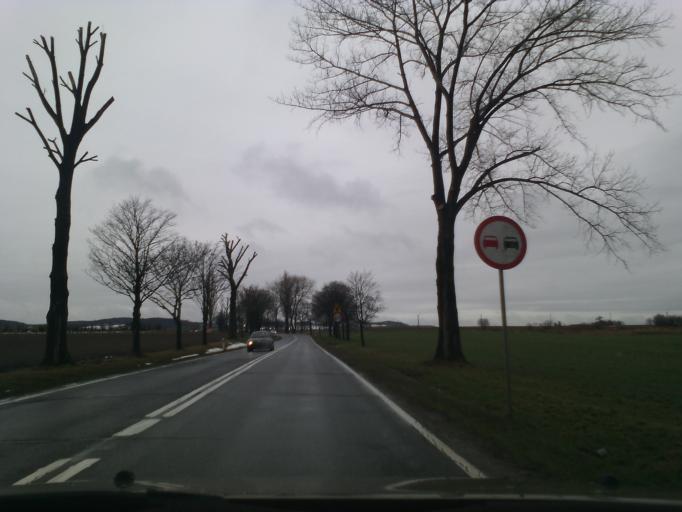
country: PL
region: Lower Silesian Voivodeship
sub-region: Powiat swidnicki
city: Swidnica
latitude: 50.8385
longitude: 16.4209
